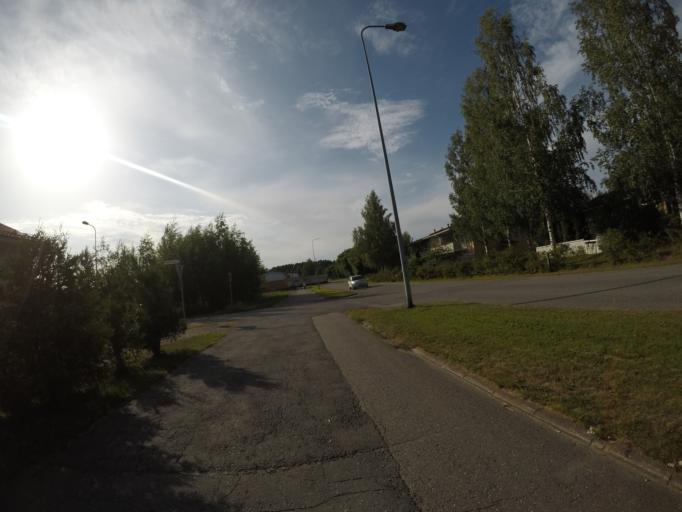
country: FI
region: Haeme
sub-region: Haemeenlinna
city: Haemeenlinna
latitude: 60.9835
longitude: 24.4257
